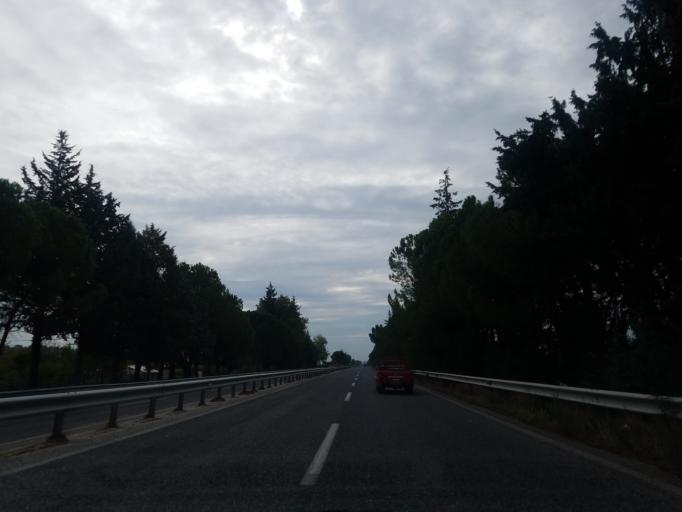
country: GR
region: Thessaly
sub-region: Trikala
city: Vasiliki
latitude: 39.6486
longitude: 21.6862
